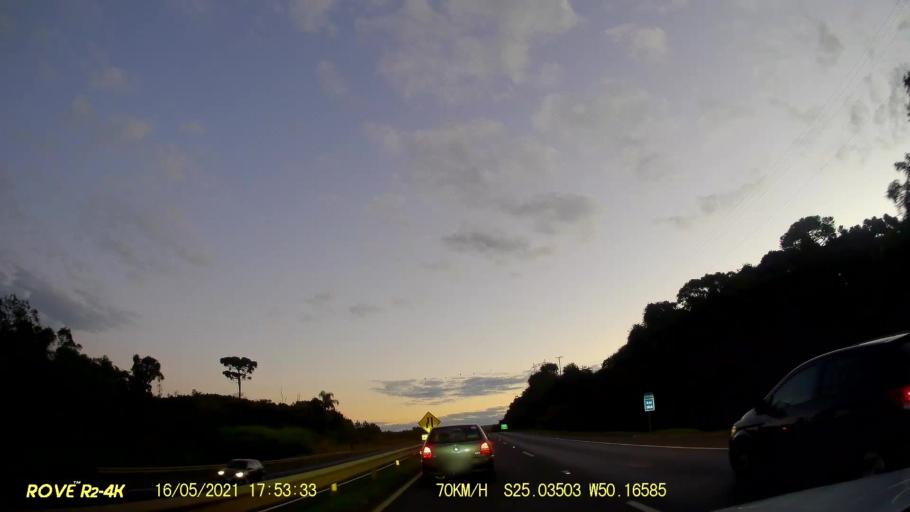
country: BR
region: Parana
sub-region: Ponta Grossa
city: Ponta Grossa
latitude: -25.0350
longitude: -50.1659
